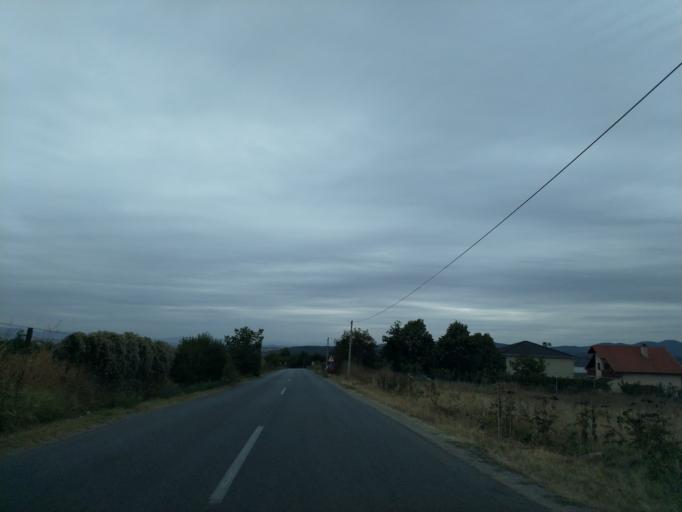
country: RS
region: Central Serbia
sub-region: Pomoravski Okrug
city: Jagodina
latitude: 43.9939
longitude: 21.2243
